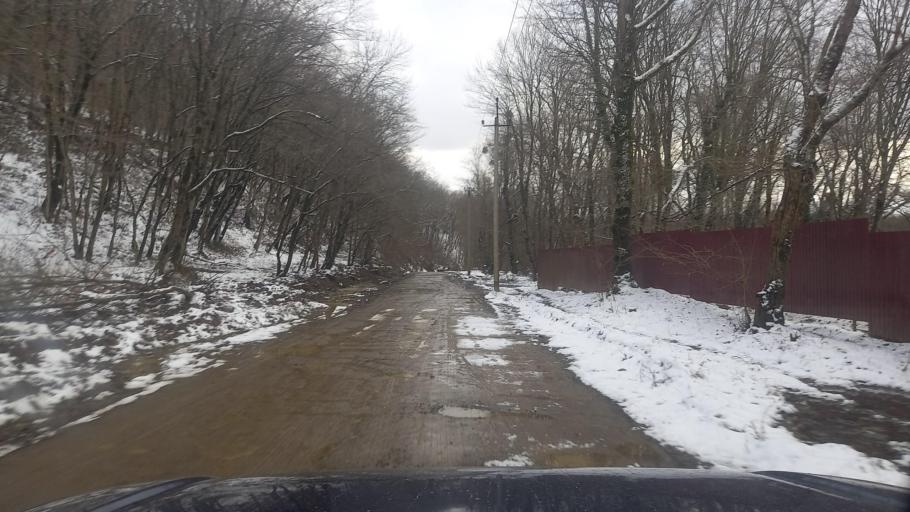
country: RU
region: Krasnodarskiy
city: Smolenskaya
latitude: 44.7016
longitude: 38.8266
